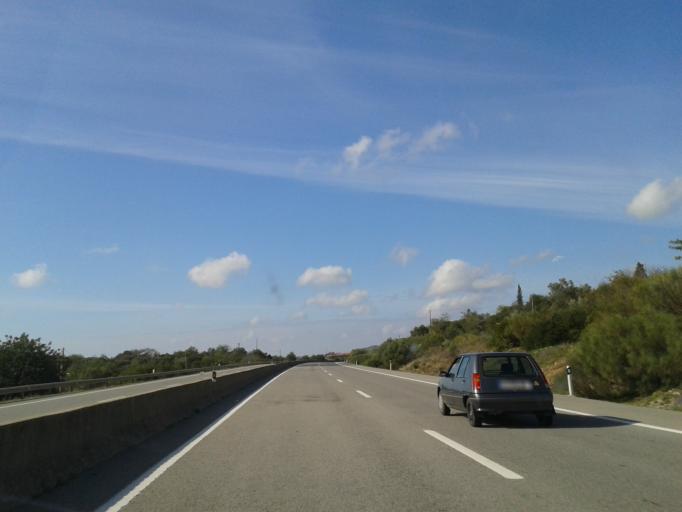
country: PT
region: Faro
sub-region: Olhao
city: Olhao
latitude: 37.0913
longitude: -7.8621
